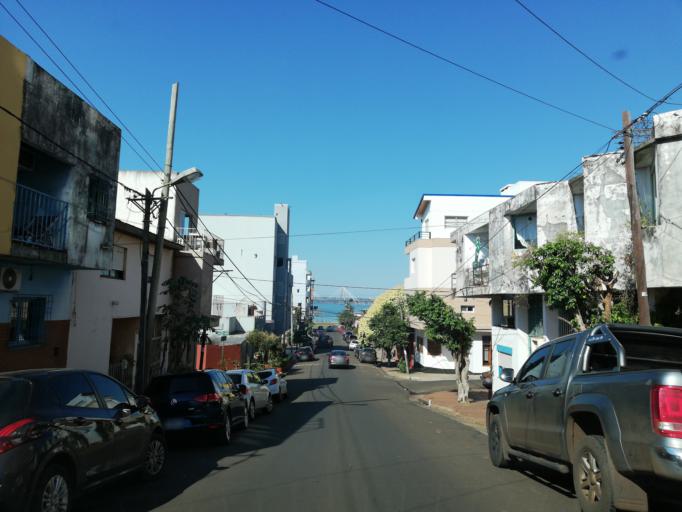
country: AR
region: Misiones
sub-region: Departamento de Capital
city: Posadas
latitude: -27.3668
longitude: -55.8867
